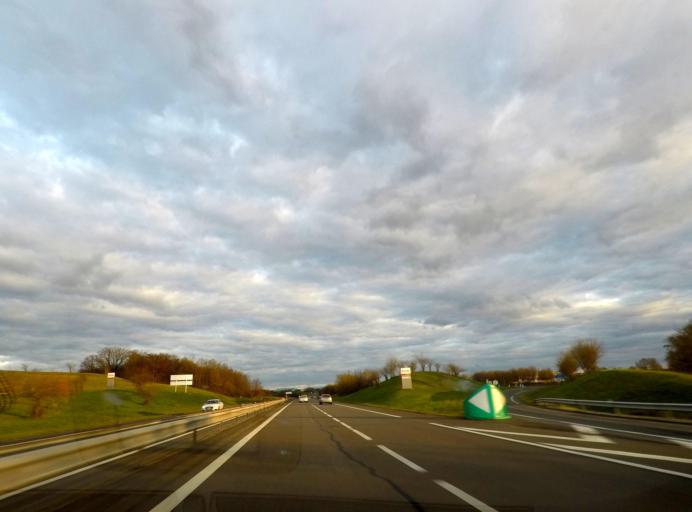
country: FR
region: Rhone-Alpes
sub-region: Departement de l'Ain
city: Saint-Cyr-sur-Menthon
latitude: 46.2792
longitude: 4.9814
